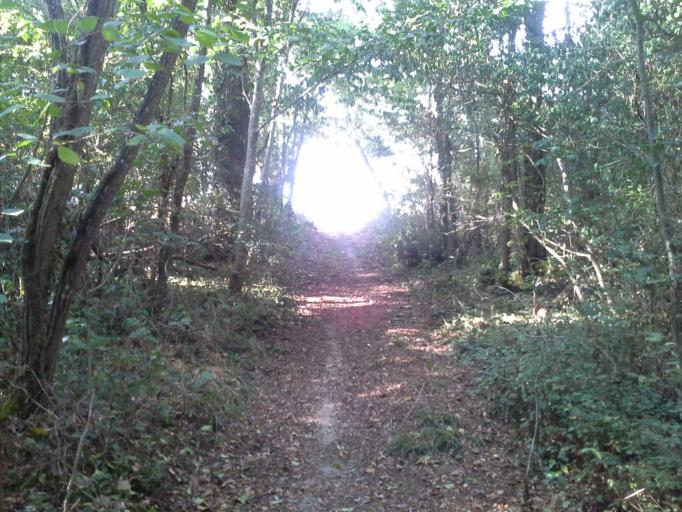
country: FR
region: Centre
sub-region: Departement du Loir-et-Cher
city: Villiers-sur-Loir
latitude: 47.8188
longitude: 1.0017
